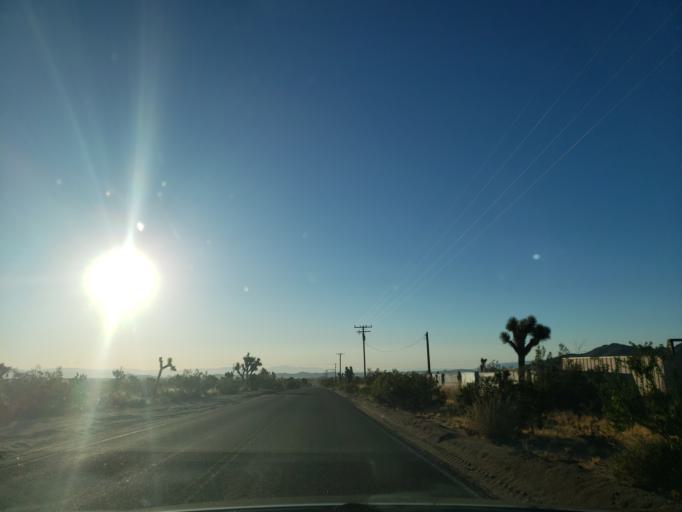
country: US
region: California
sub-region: San Bernardino County
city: Joshua Tree
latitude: 34.1930
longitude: -116.3727
